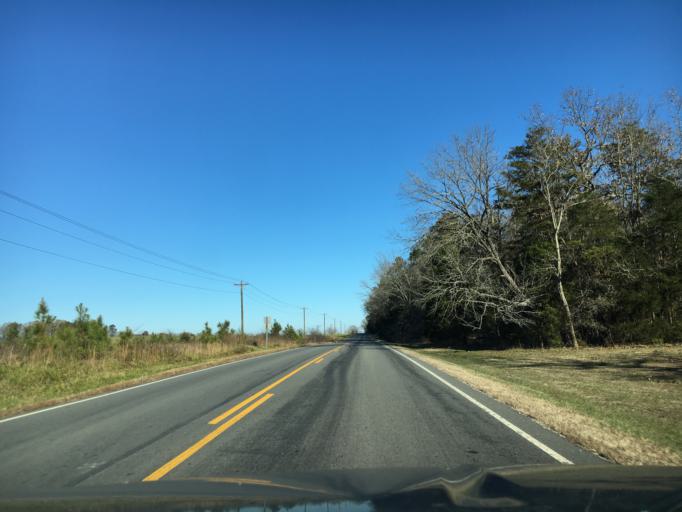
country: US
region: Virginia
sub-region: Buckingham County
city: Buckingham
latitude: 37.5288
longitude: -78.6161
